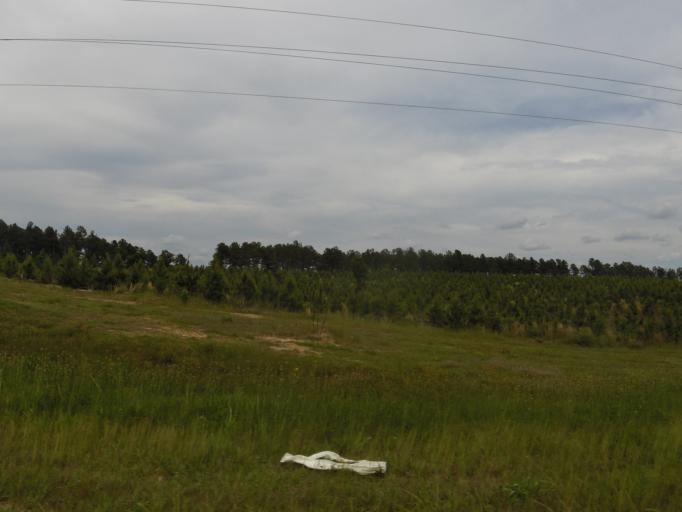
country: US
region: Georgia
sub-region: Jefferson County
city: Wrens
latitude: 33.3068
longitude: -82.4439
